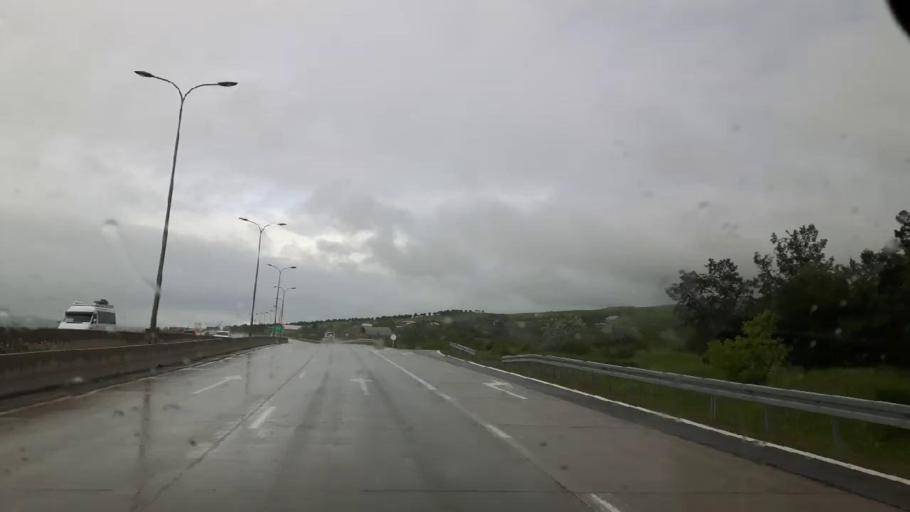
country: GE
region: Shida Kartli
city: Gori
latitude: 42.0242
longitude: 44.2271
